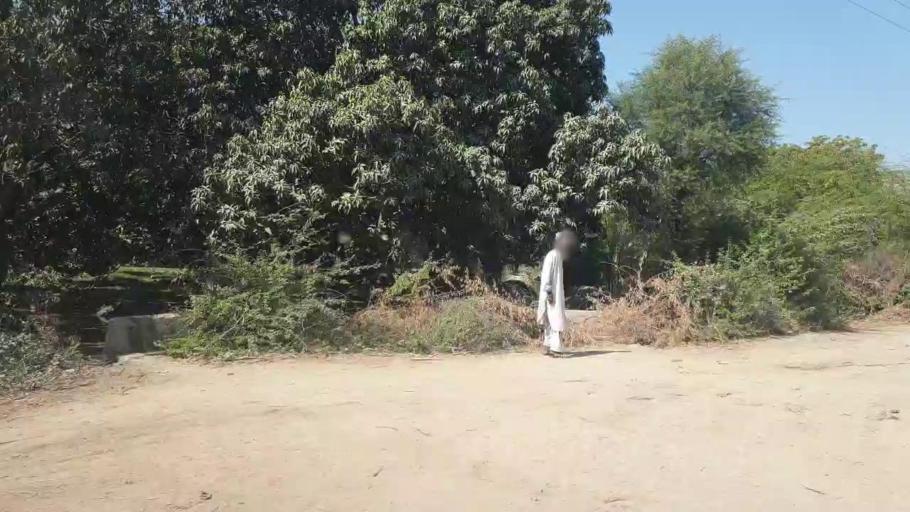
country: PK
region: Sindh
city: Digri
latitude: 25.2514
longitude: 69.2292
